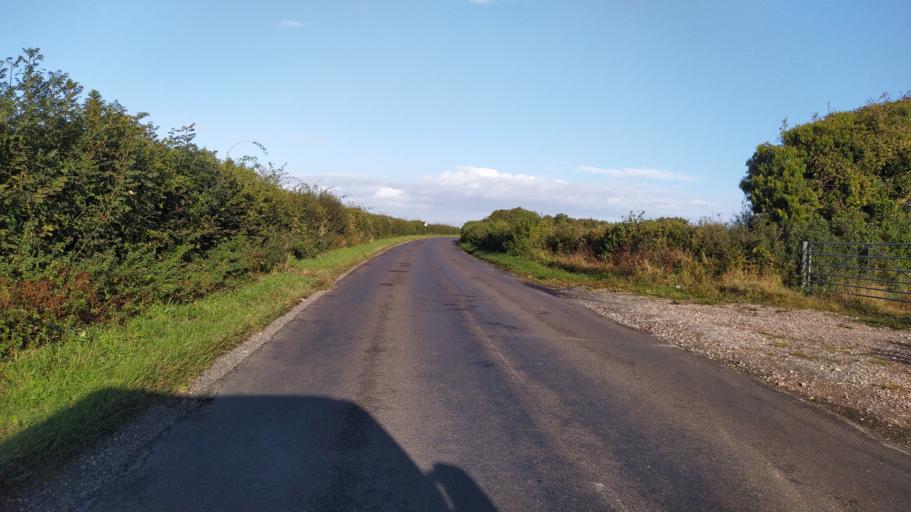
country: GB
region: England
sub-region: Dorset
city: Wimborne Minster
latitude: 50.8916
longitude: -2.0109
